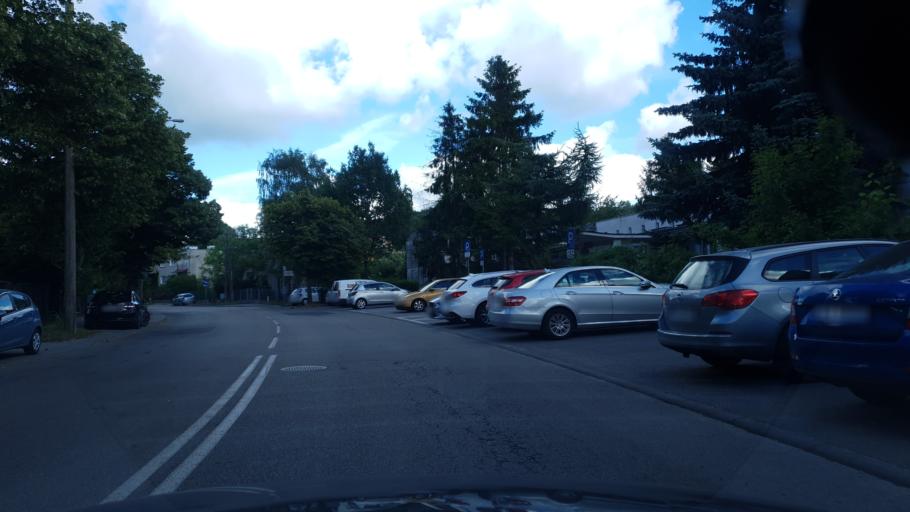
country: PL
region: Pomeranian Voivodeship
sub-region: Gdynia
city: Gdynia
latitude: 54.4896
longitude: 18.5460
